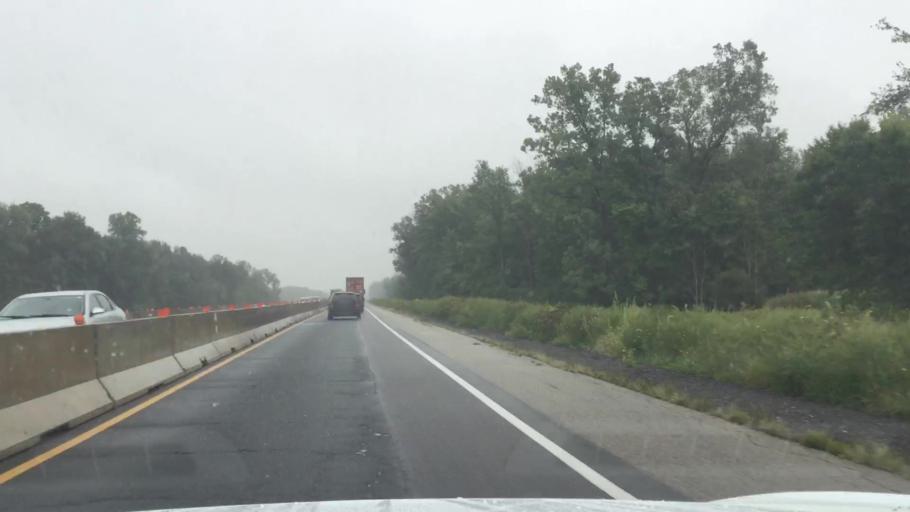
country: CA
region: Ontario
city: Delaware
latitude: 42.7969
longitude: -81.3442
